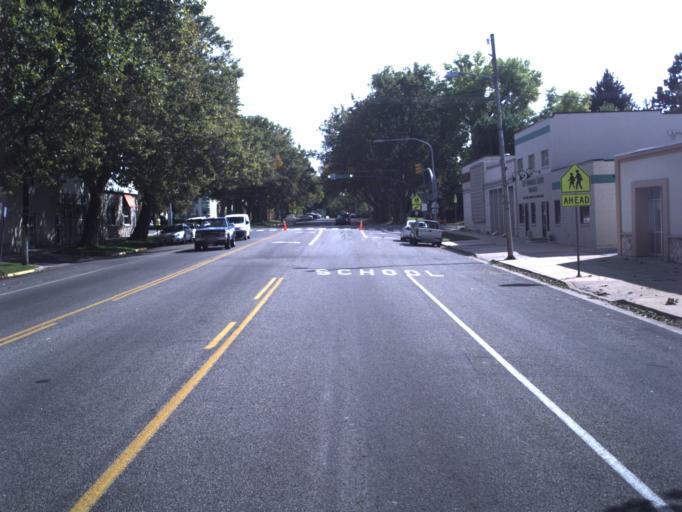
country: US
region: Utah
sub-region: Davis County
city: Farmington
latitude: 40.9814
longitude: -111.8876
